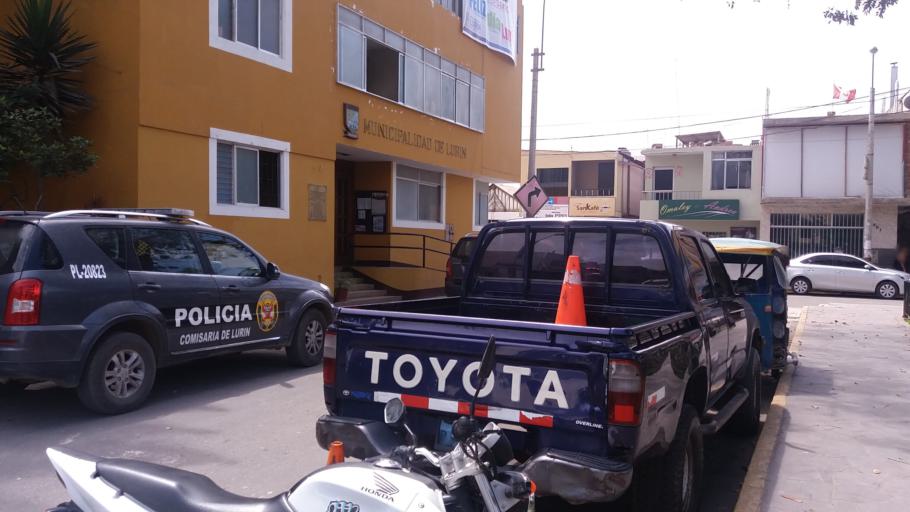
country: PE
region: Lima
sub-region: Lima
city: Punta Hermosa
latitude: -12.2735
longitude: -76.8692
